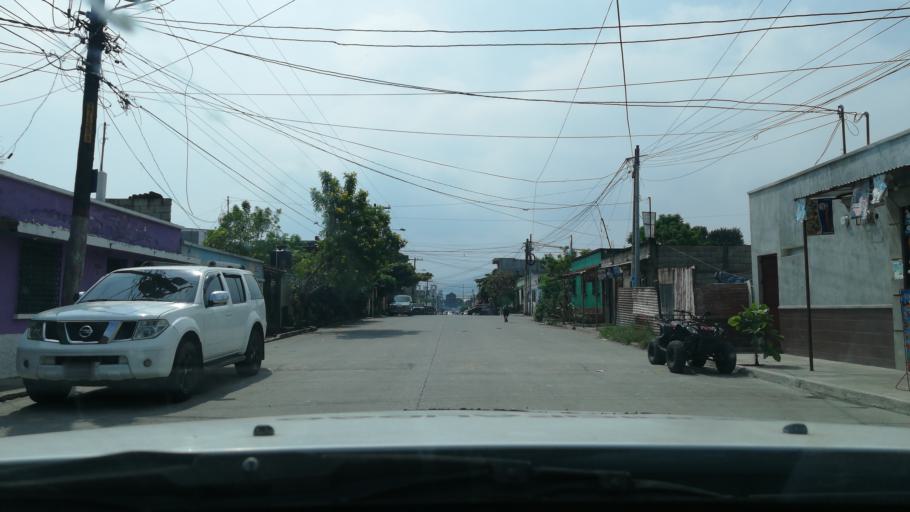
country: GT
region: Guatemala
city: Petapa
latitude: 14.5091
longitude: -90.5649
